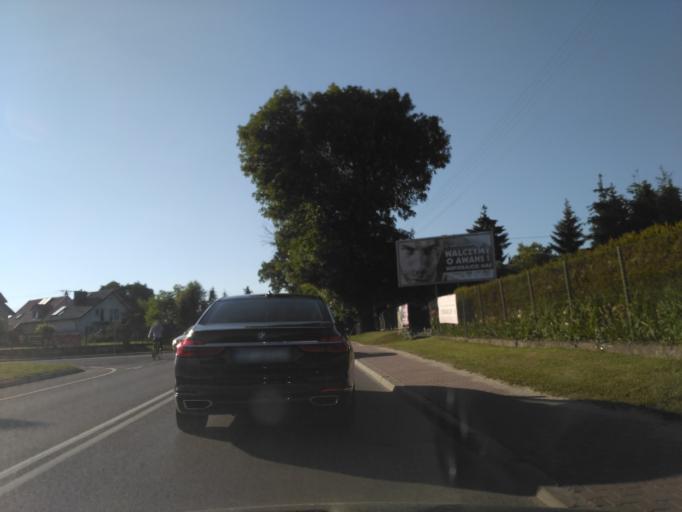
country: PL
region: Lublin Voivodeship
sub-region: Powiat lubelski
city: Bychawa
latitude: 51.0186
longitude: 22.5242
